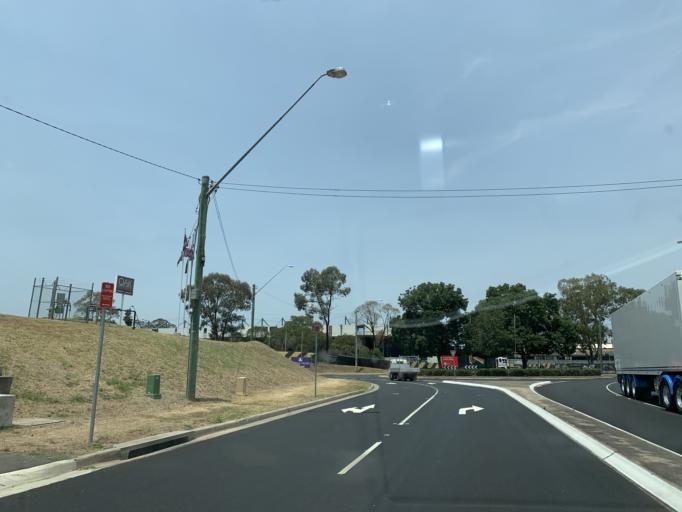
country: AU
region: New South Wales
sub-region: Blacktown
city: Doonside
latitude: -33.8017
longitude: 150.8700
